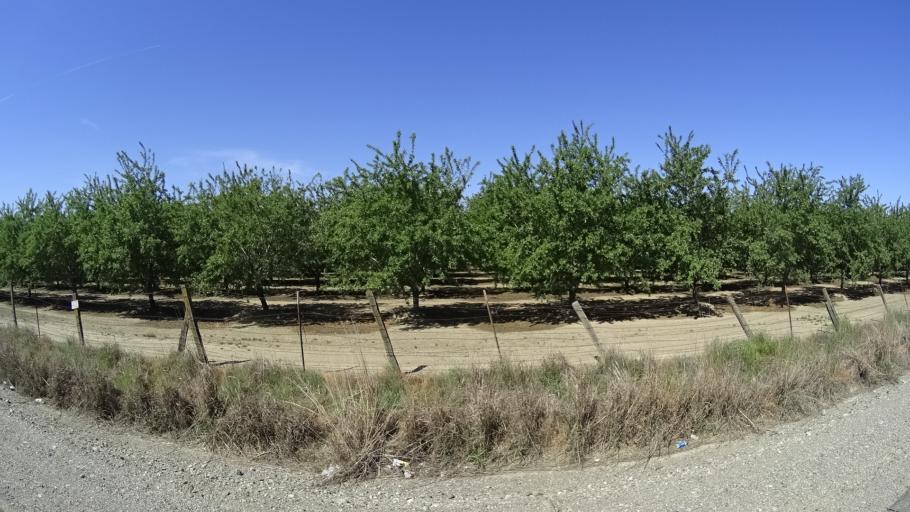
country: US
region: California
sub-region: Glenn County
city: Orland
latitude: 39.7377
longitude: -122.1410
